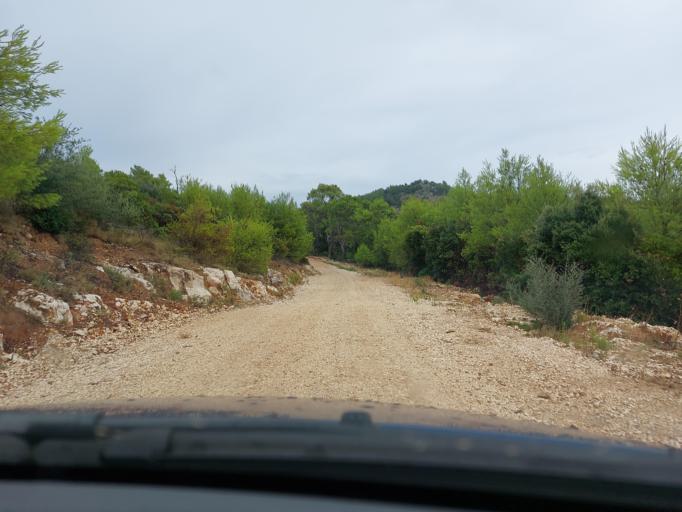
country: HR
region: Dubrovacko-Neretvanska
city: Smokvica
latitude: 42.7437
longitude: 16.9138
